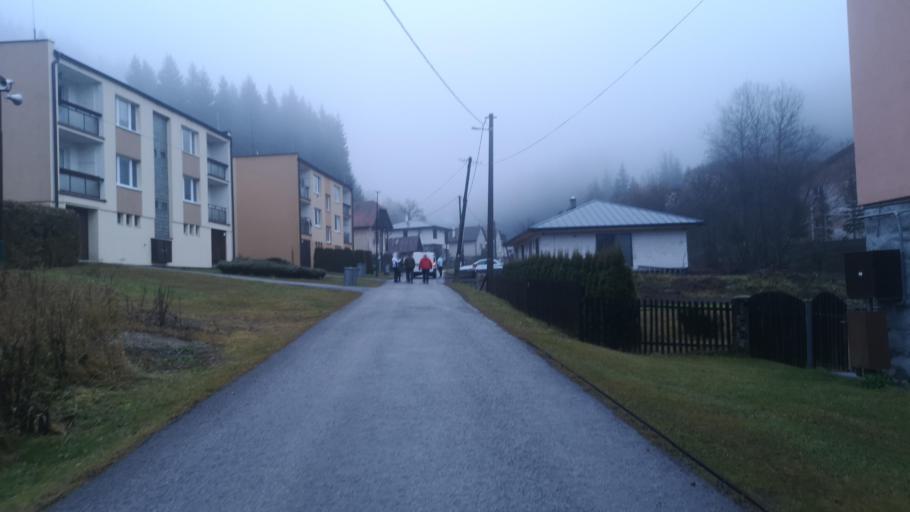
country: SK
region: Banskobystricky
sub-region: Okres Ziar nad Hronom
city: Kremnica
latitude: 48.7554
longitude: 18.9316
